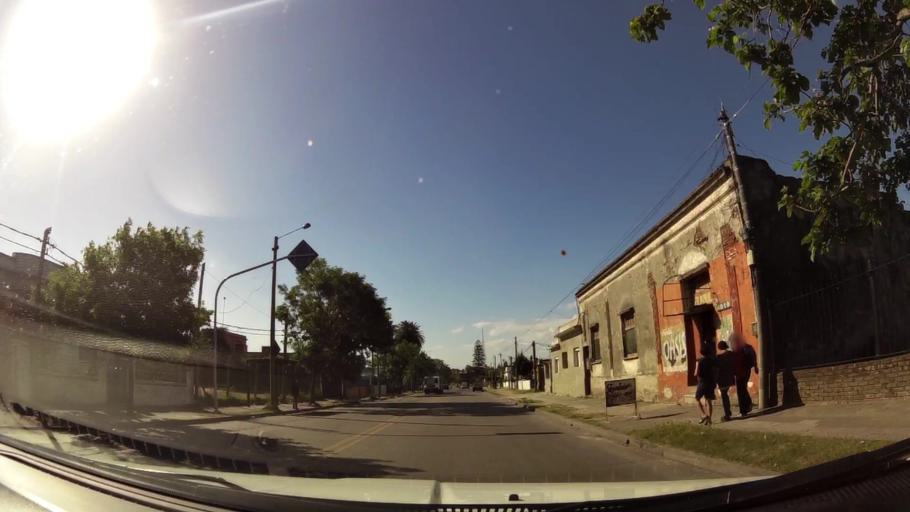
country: UY
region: Montevideo
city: Montevideo
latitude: -34.8360
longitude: -56.1501
